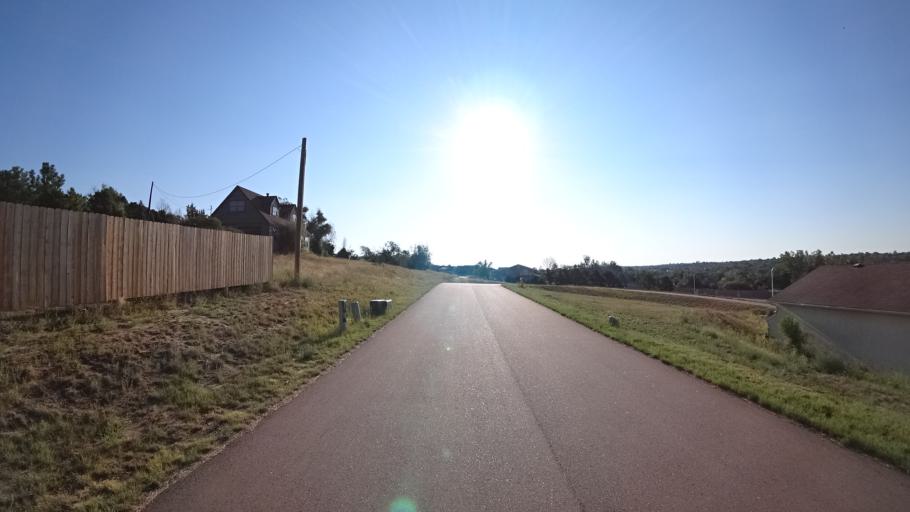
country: US
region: Colorado
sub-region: El Paso County
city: Cimarron Hills
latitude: 38.9341
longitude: -104.7721
